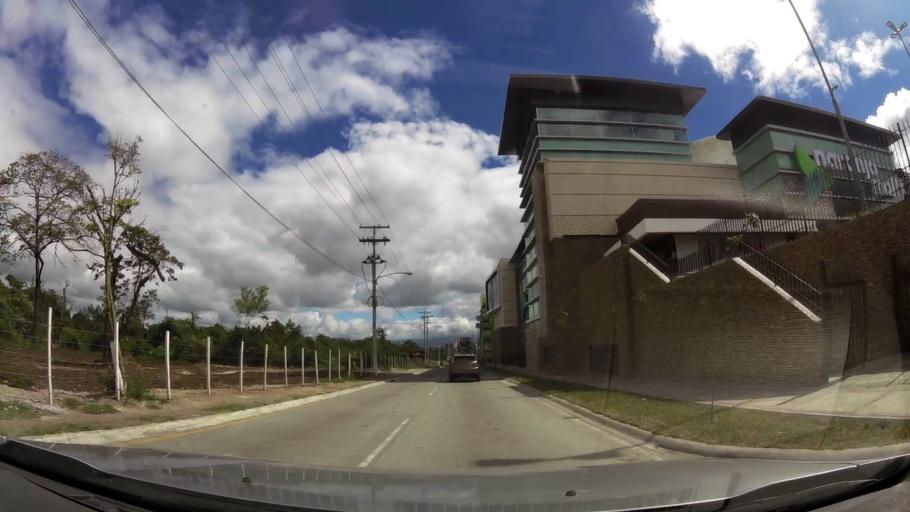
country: GT
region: Guatemala
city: Guatemala City
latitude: 14.6514
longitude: -90.5433
